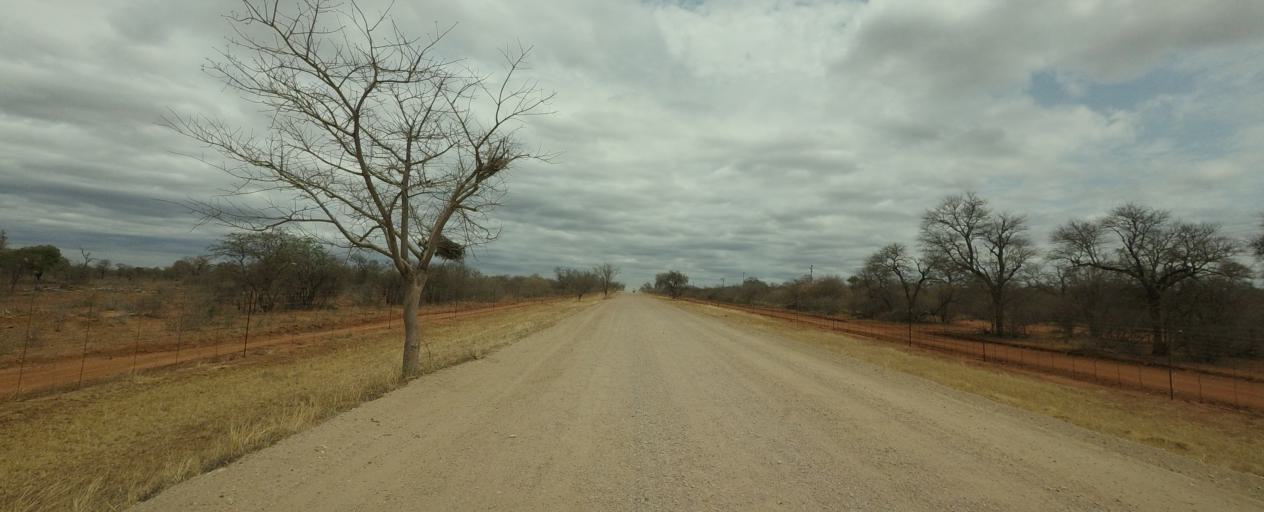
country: BW
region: Central
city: Mathathane
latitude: -22.6864
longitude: 28.6473
